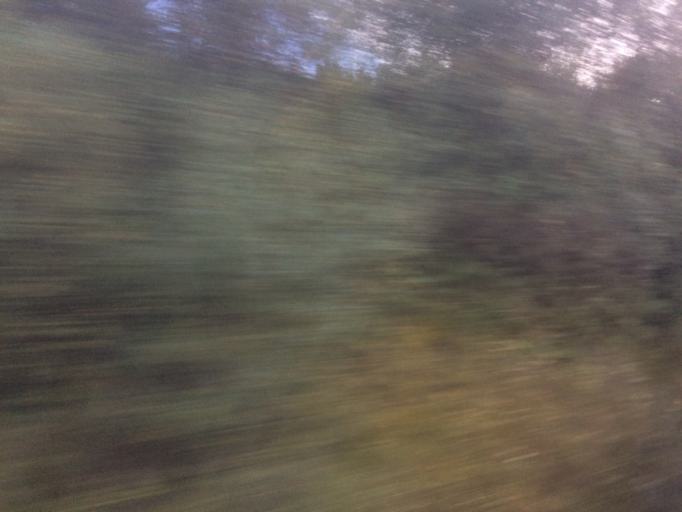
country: GB
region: Scotland
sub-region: North Lanarkshire
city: Kilsyth
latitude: 55.9648
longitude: -4.0243
